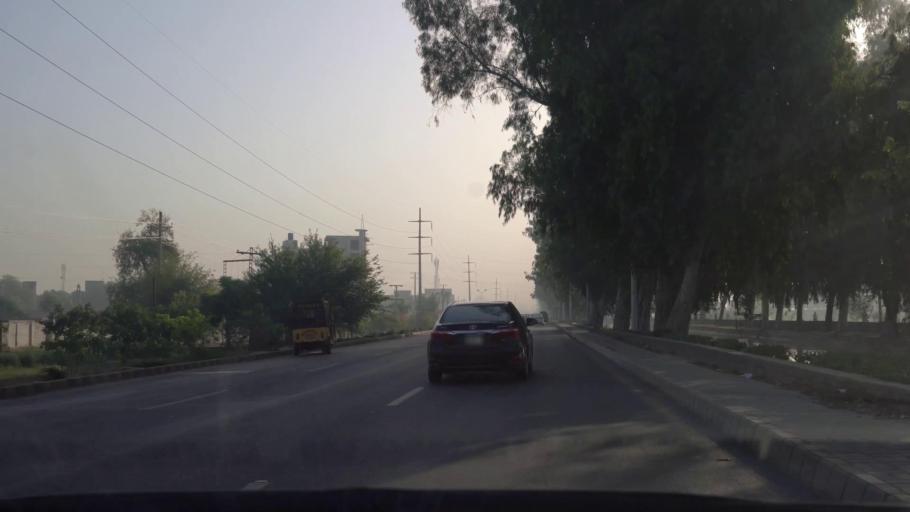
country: PK
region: Punjab
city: Faisalabad
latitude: 31.4534
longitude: 73.1554
